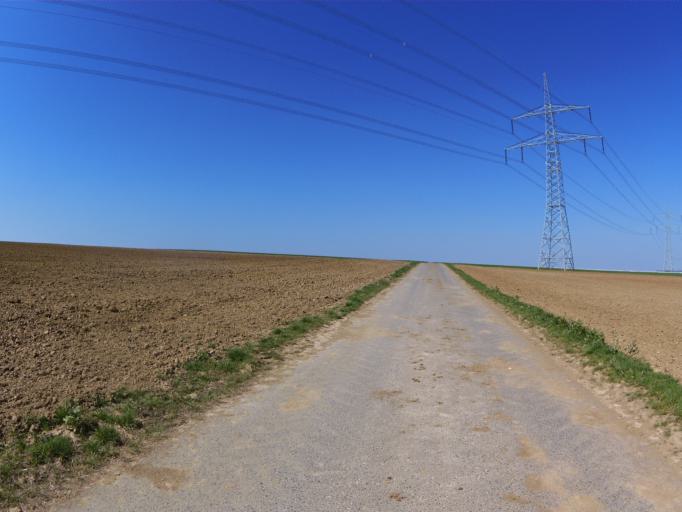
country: DE
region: Bavaria
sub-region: Regierungsbezirk Unterfranken
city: Biebelried
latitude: 49.8168
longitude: 10.0841
